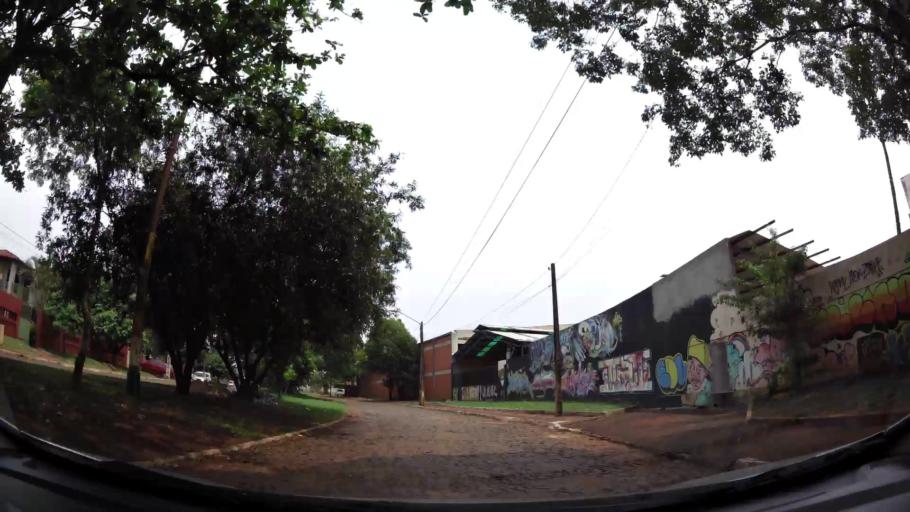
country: PY
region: Alto Parana
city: Presidente Franco
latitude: -25.5520
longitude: -54.6154
